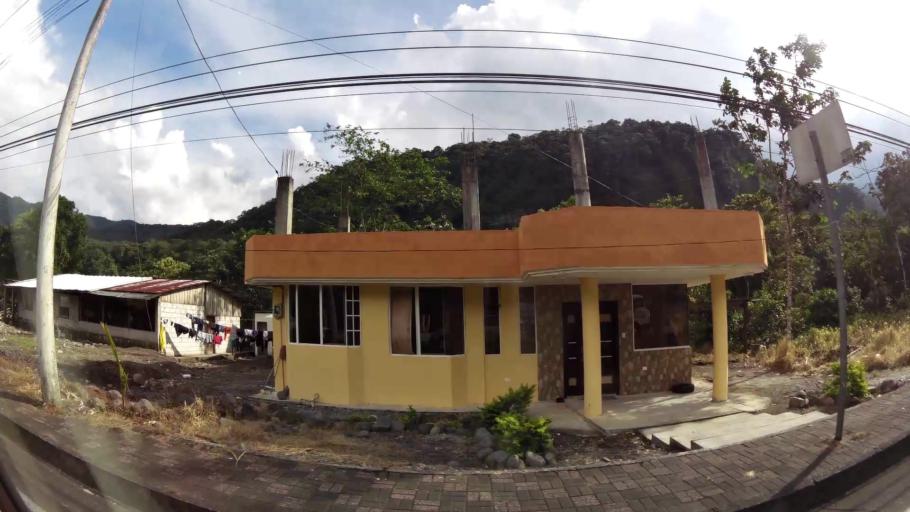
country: EC
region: Tungurahua
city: Banos
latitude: -1.4142
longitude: -78.2169
